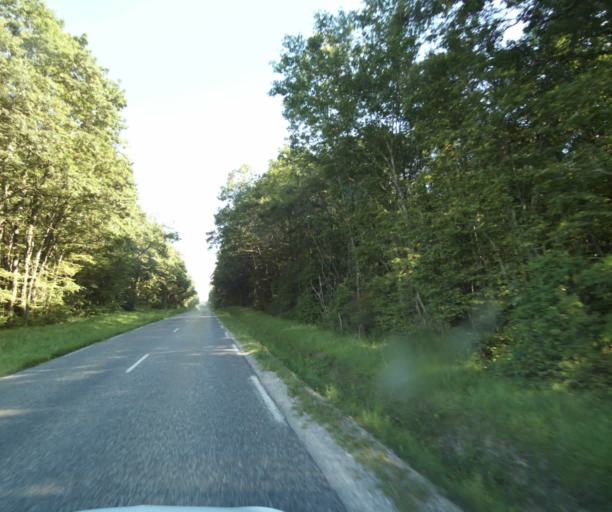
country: FR
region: Rhone-Alpes
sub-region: Departement de la Haute-Savoie
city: Messery
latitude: 46.3299
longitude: 6.2922
